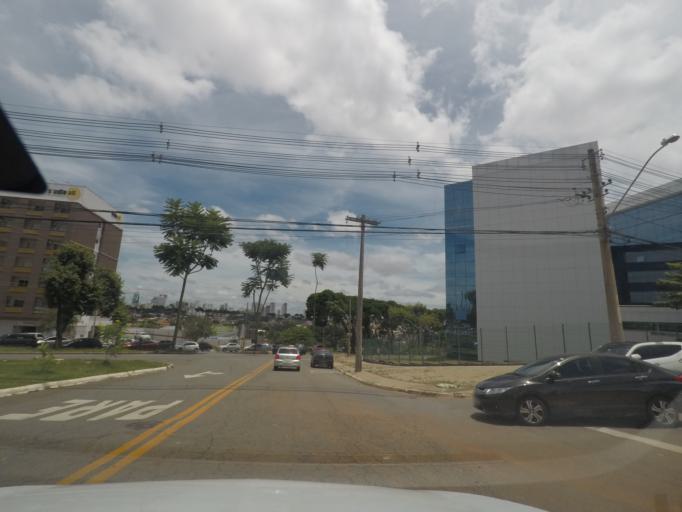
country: BR
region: Goias
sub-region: Goiania
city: Goiania
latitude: -16.6890
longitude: -49.2405
